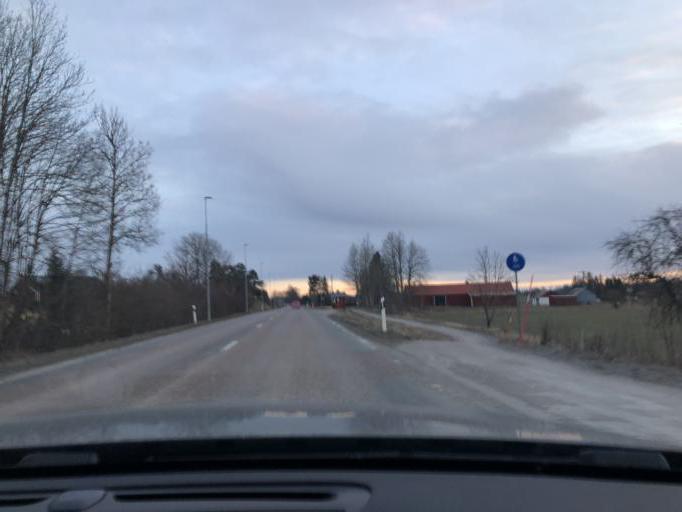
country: SE
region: Uppsala
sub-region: Uppsala Kommun
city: Gamla Uppsala
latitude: 59.9130
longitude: 17.6431
